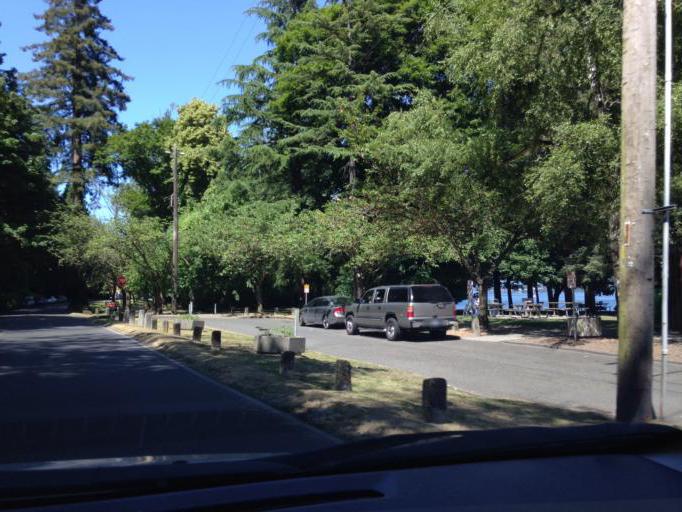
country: US
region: Washington
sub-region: King County
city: Seattle
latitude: 47.6099
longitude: -122.2829
